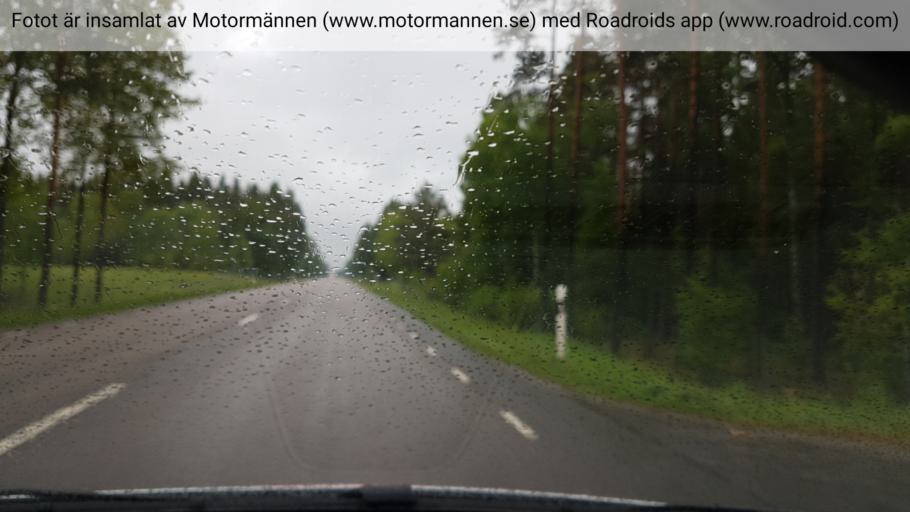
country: SE
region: Vaestra Goetaland
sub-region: Falkopings Kommun
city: Falkoeping
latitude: 58.0346
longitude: 13.5475
